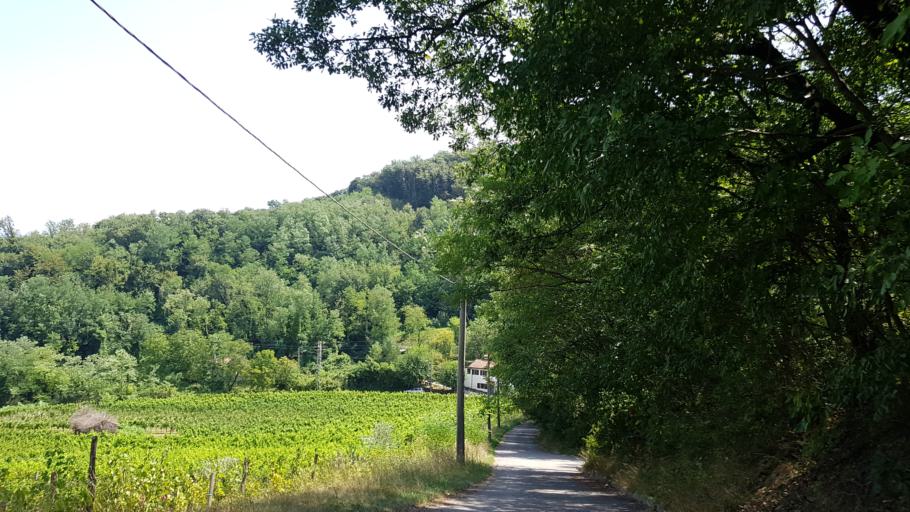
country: IT
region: Friuli Venezia Giulia
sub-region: Provincia di Udine
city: Corno di Rosazzo
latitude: 45.9786
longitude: 13.4572
